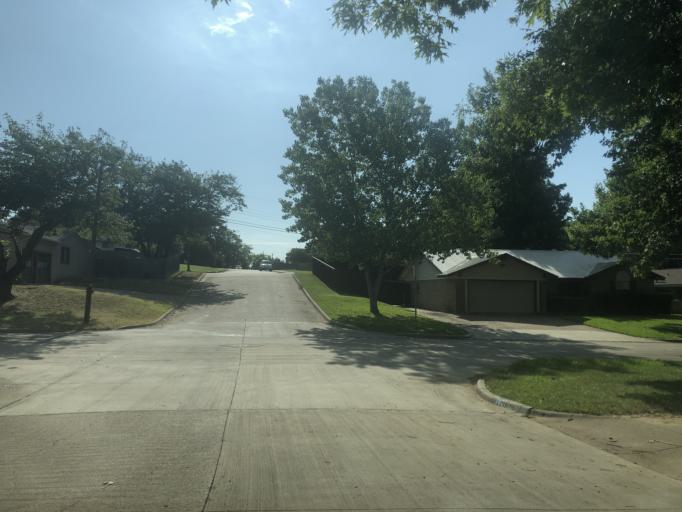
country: US
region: Texas
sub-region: Dallas County
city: Grand Prairie
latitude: 32.7555
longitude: -97.0229
